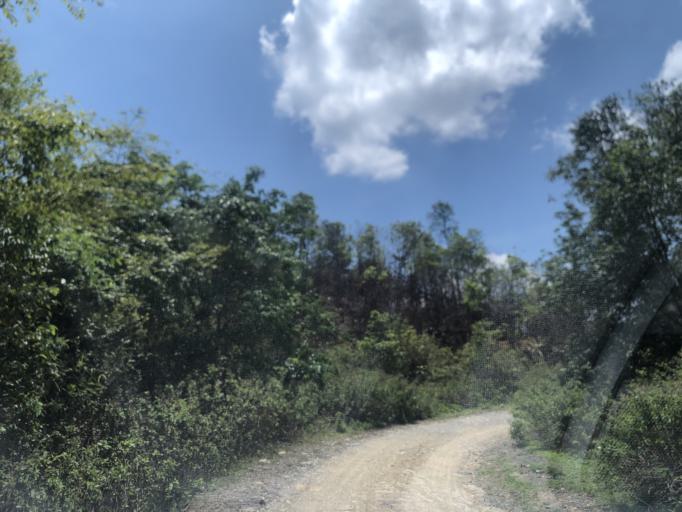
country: LA
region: Phongsali
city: Phongsali
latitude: 21.4402
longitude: 102.1631
